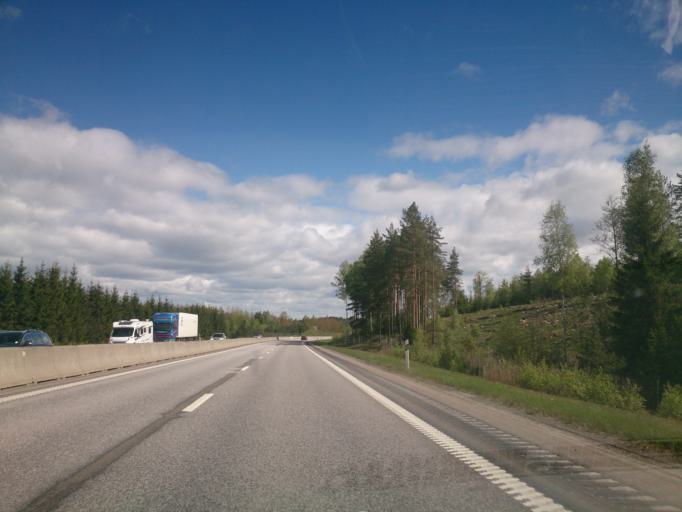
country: SE
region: OEstergoetland
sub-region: Norrkopings Kommun
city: Kimstad
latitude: 58.5199
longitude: 16.0015
